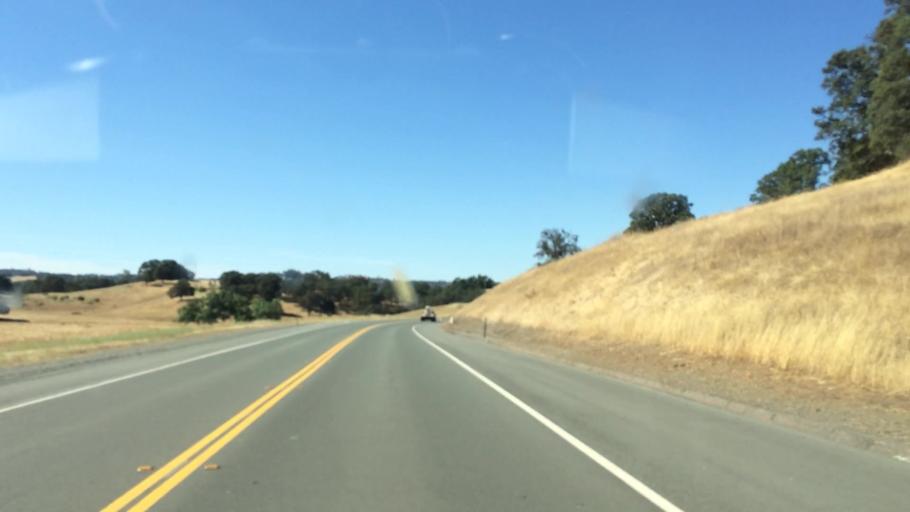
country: US
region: California
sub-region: Amador County
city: Plymouth
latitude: 38.4481
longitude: -120.8727
